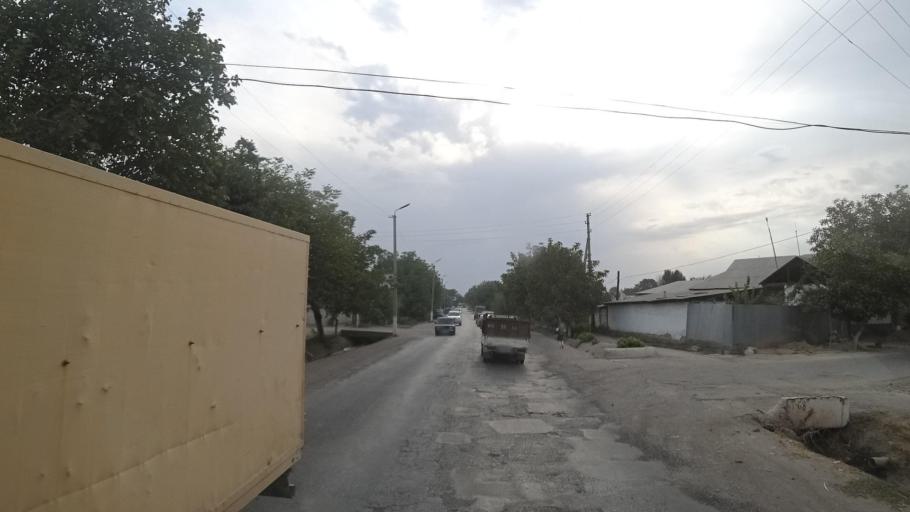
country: KG
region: Jalal-Abad
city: Massy
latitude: 41.0638
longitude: 72.6446
